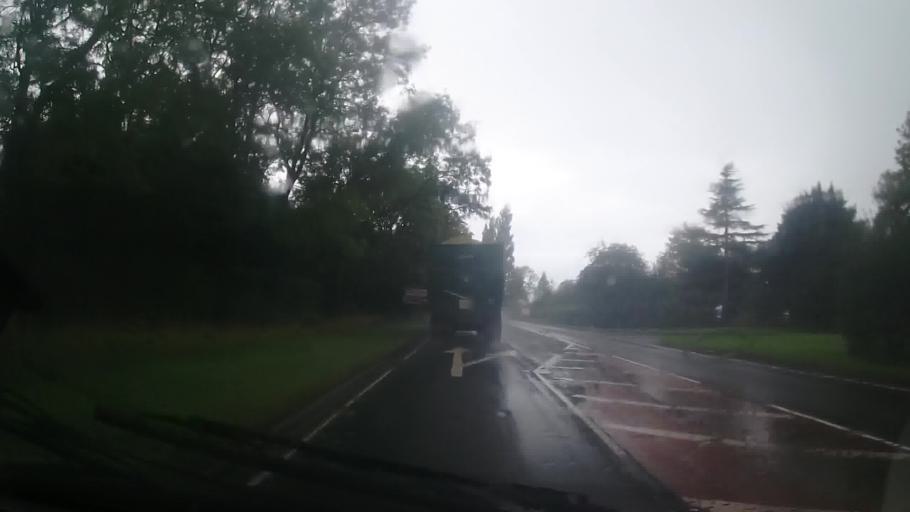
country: GB
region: England
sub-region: Worcestershire
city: Evesham
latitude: 52.1226
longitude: -2.0036
